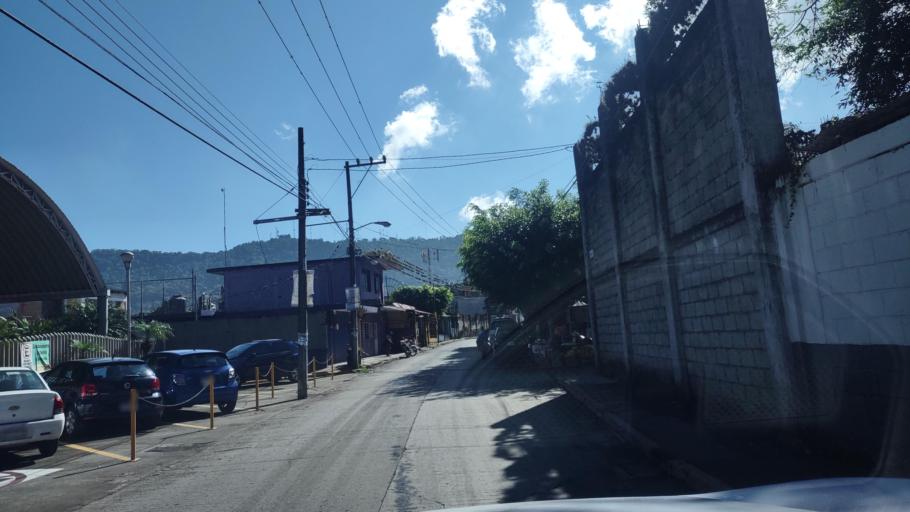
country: MX
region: Veracruz
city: Cuautlapan
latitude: 18.8732
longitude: -97.0228
